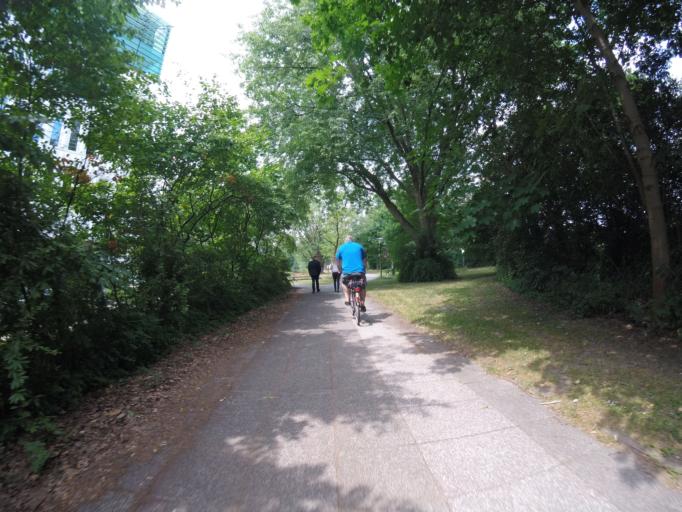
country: DE
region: Hamburg
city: Barmbek-Nord
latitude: 53.6040
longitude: 10.0286
